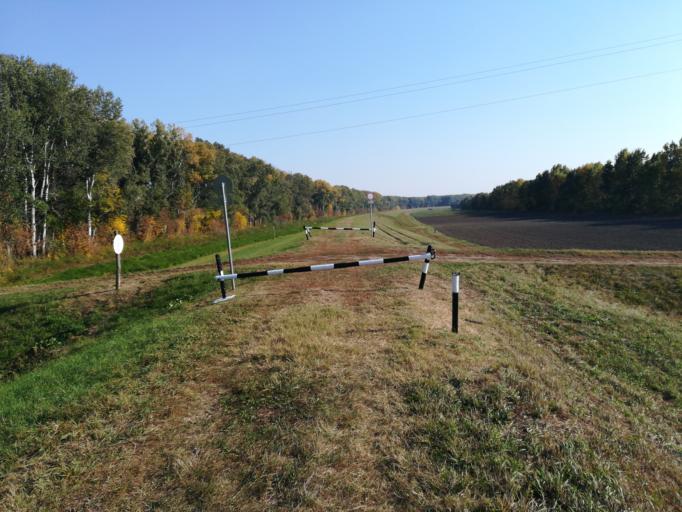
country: HU
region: Bacs-Kiskun
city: Tiszakecske
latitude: 46.9349
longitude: 20.1444
